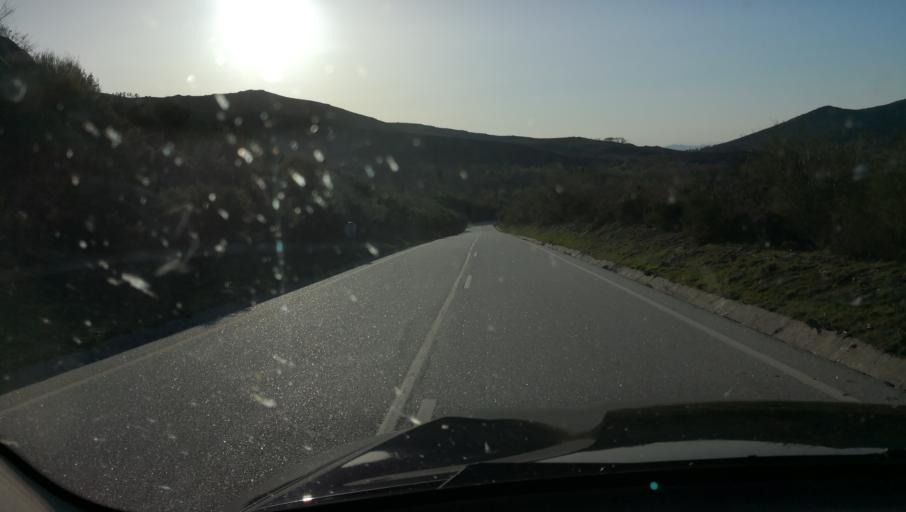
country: PT
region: Vila Real
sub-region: Vila Real
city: Vila Real
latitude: 41.3636
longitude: -7.7976
